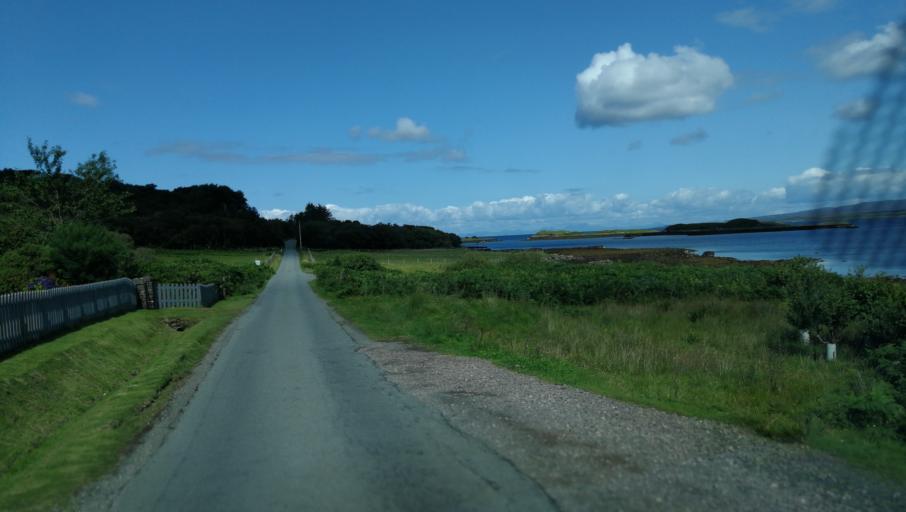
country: GB
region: Scotland
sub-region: Highland
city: Isle of Skye
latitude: 57.4436
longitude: -6.6418
